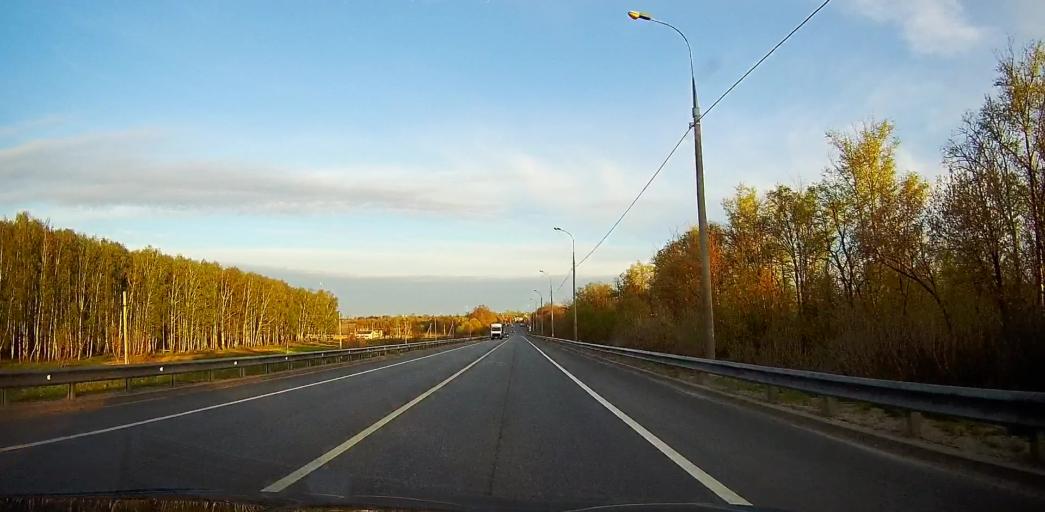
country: RU
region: Moskovskaya
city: Troitskoye
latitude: 55.2327
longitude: 38.5509
